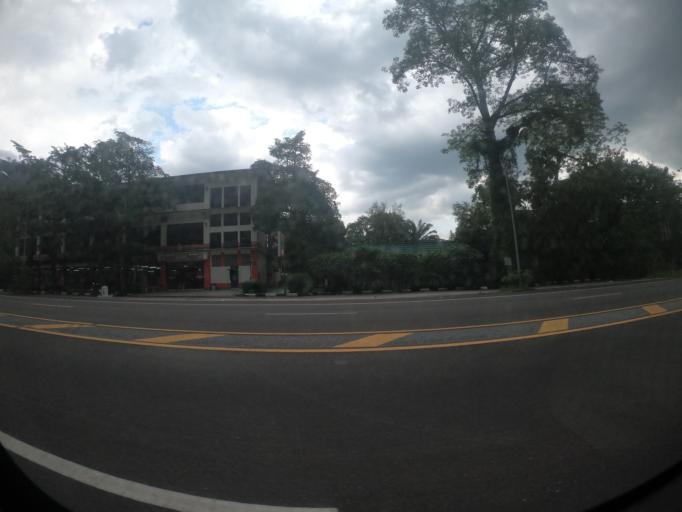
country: TH
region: Nakhon Nayok
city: Nakhon Nayok
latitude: 14.3262
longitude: 101.3167
